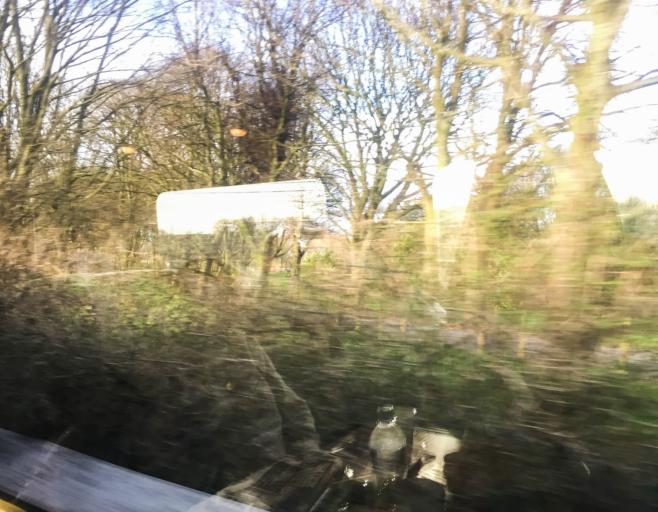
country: GB
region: England
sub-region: Cumbria
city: Carlisle
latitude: 54.8985
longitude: -2.9464
